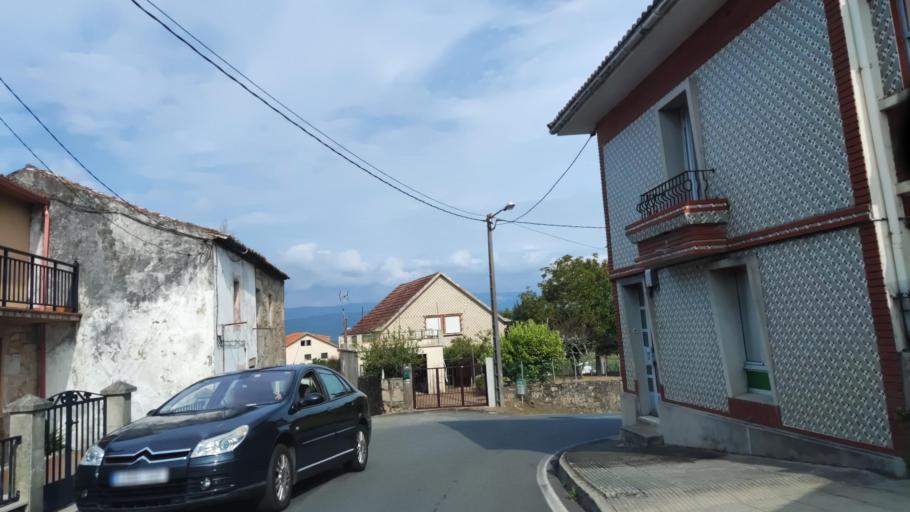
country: ES
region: Galicia
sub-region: Provincia da Coruna
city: Rianxo
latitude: 42.6479
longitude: -8.8108
